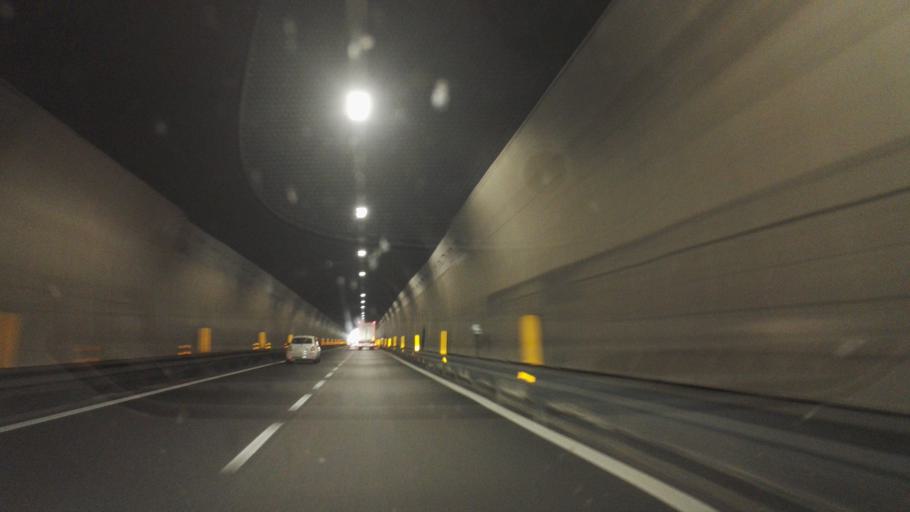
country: IT
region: Calabria
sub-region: Provincia di Cosenza
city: Rosario
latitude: 39.2955
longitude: 16.2373
